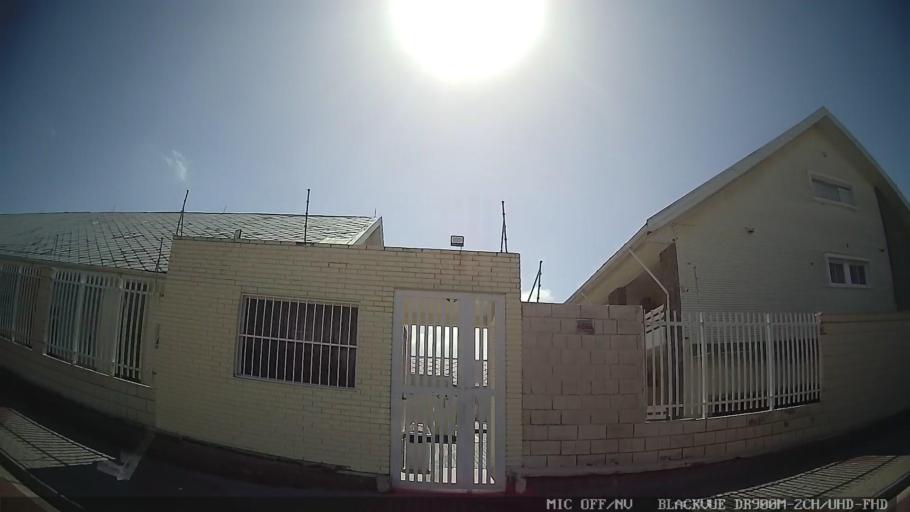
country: BR
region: Sao Paulo
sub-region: Itanhaem
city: Itanhaem
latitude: -24.1660
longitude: -46.7503
